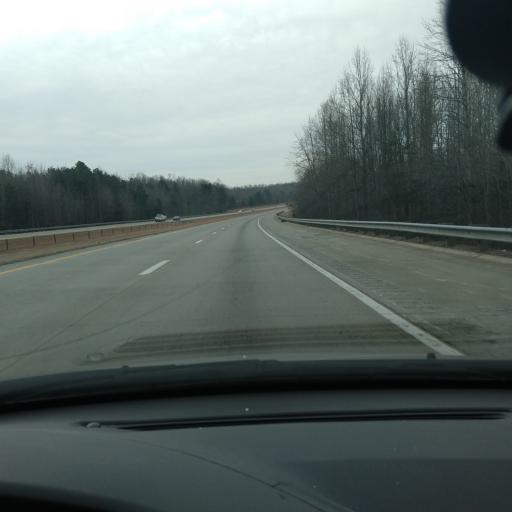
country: US
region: North Carolina
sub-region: Davidson County
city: Midway
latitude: 35.9310
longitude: -80.2319
